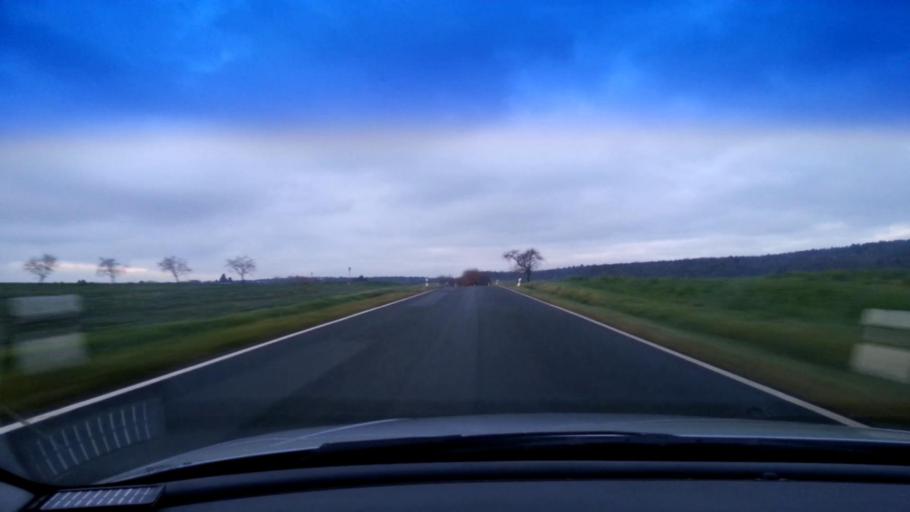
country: DE
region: Bavaria
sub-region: Upper Franconia
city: Frensdorf
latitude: 49.8280
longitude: 10.8819
